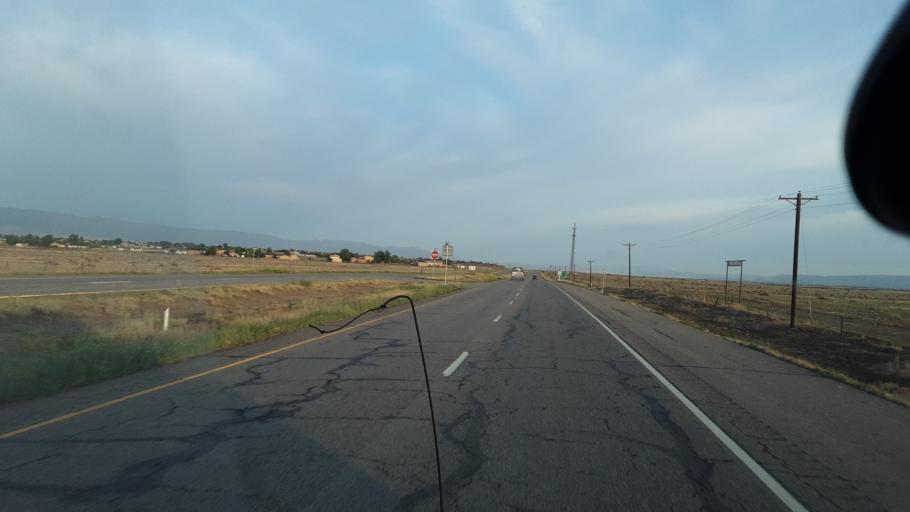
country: US
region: Colorado
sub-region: Pueblo County
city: Pueblo West
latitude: 38.3438
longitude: -104.7734
